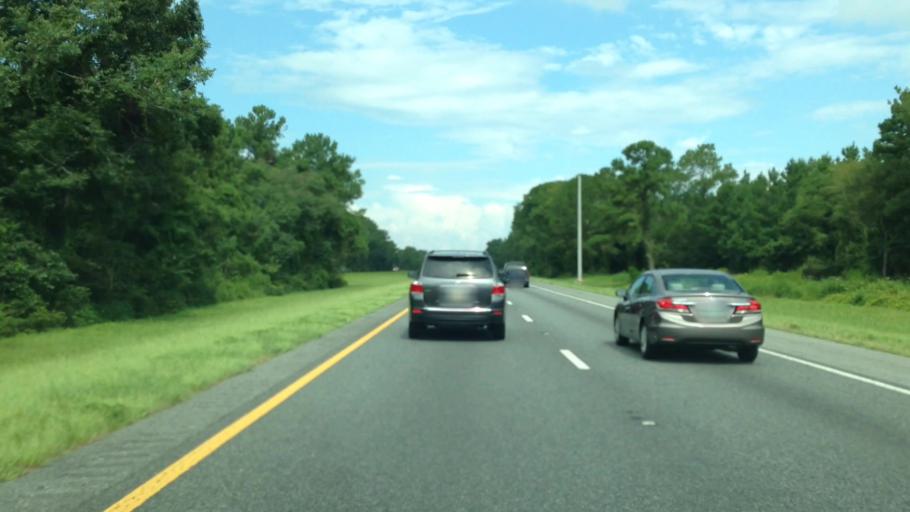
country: US
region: Florida
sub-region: Suwannee County
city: Live Oak
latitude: 30.3039
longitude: -82.9167
